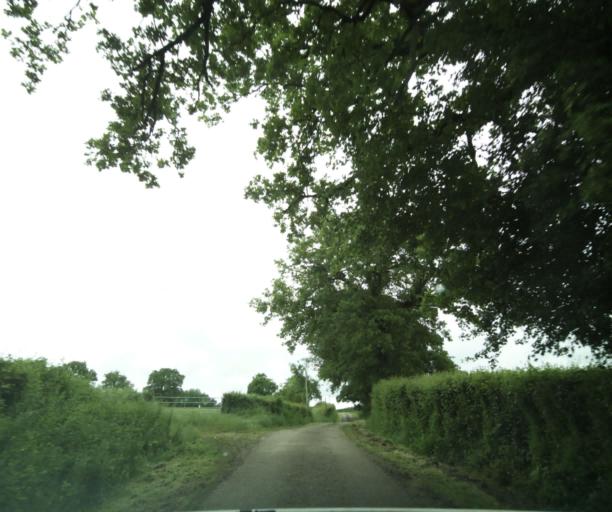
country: FR
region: Bourgogne
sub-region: Departement de Saone-et-Loire
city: Charolles
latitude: 46.4641
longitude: 4.2984
